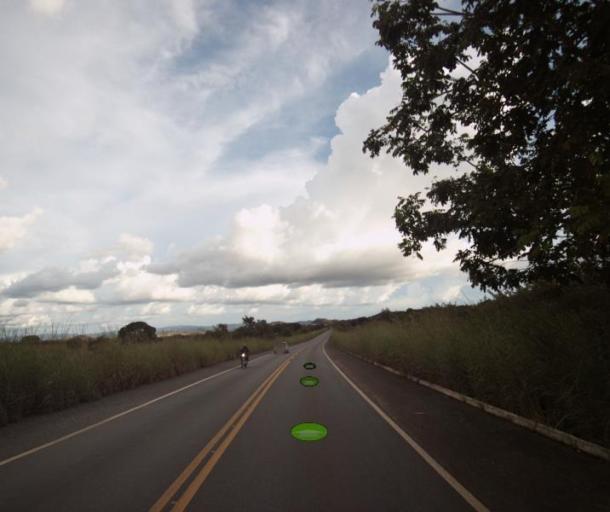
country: BR
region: Goias
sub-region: Niquelandia
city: Niquelandia
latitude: -14.6344
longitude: -48.5896
